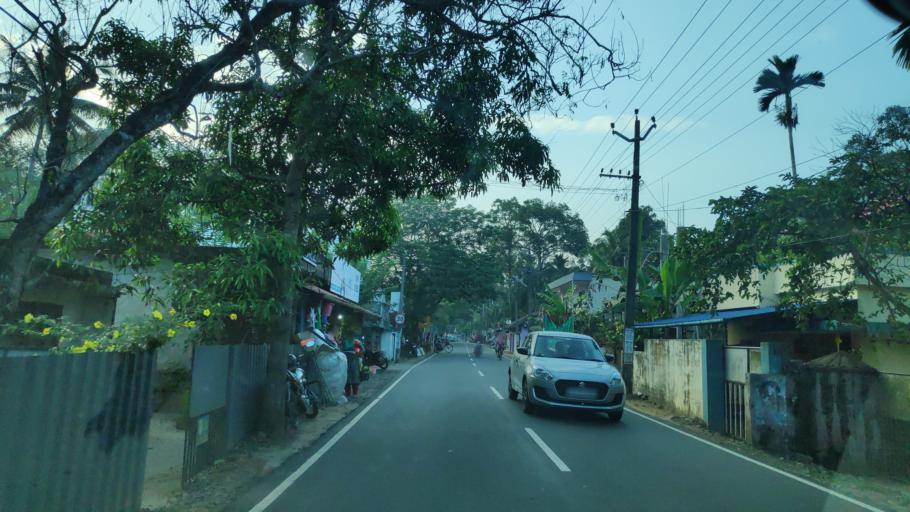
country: IN
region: Kerala
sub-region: Alappuzha
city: Shertallai
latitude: 9.6794
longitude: 76.3748
